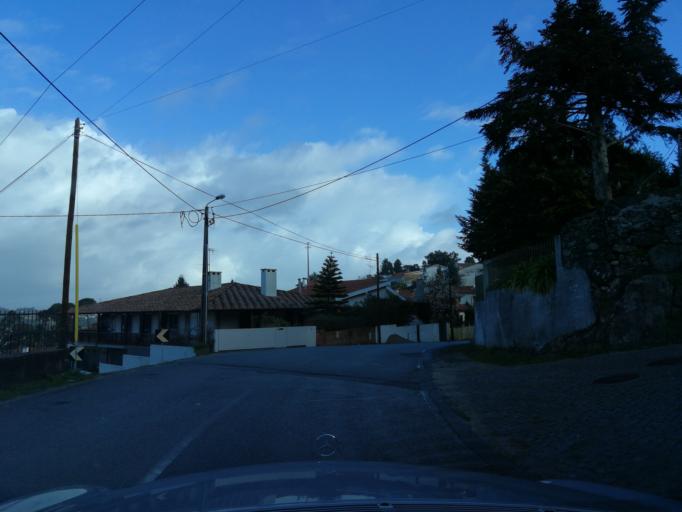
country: PT
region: Braga
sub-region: Braga
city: Braga
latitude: 41.5449
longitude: -8.3901
